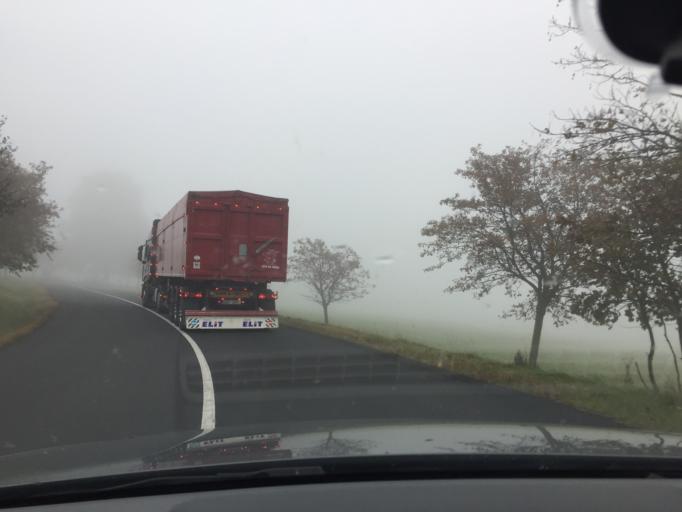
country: CZ
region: Ustecky
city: Libouchec
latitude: 50.7801
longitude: 14.0022
